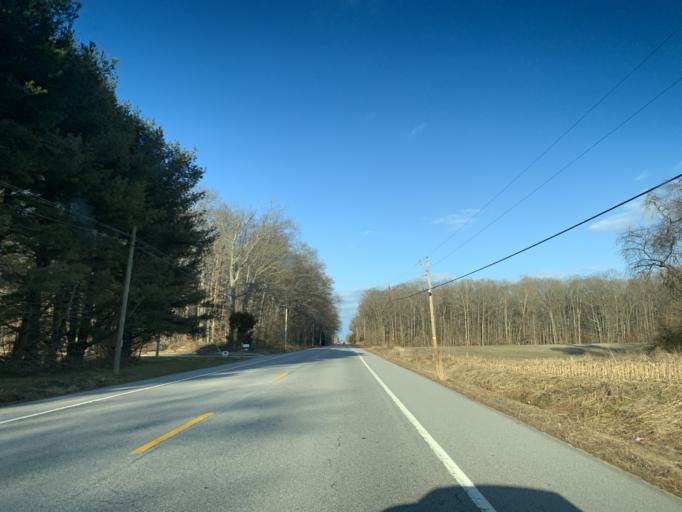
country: US
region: Maryland
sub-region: Queen Anne's County
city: Kingstown
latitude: 39.1655
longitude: -75.9339
